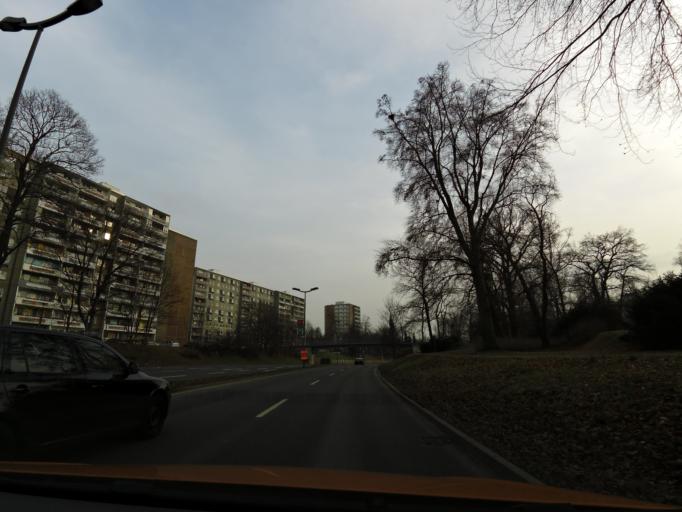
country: DE
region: Brandenburg
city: Frankfurt (Oder)
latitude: 52.3457
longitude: 14.5391
